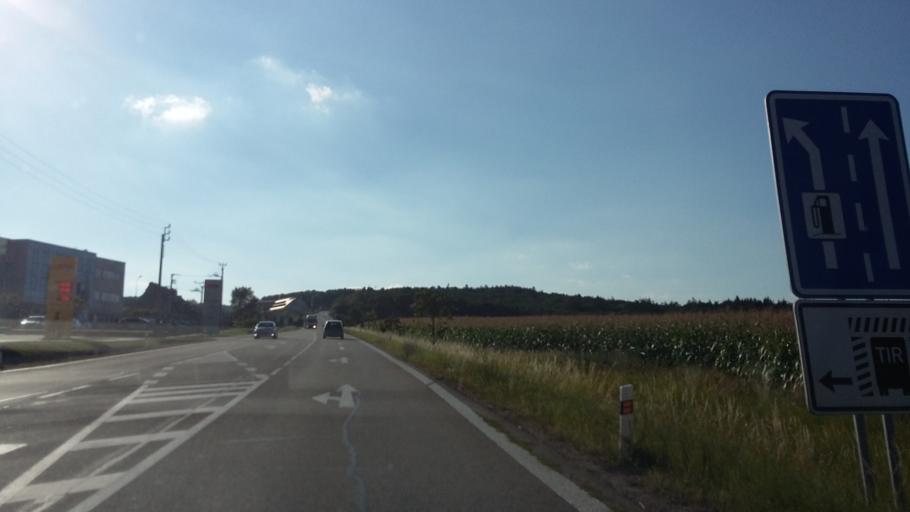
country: CZ
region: South Moravian
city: Troubsko
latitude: 49.1828
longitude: 16.4851
